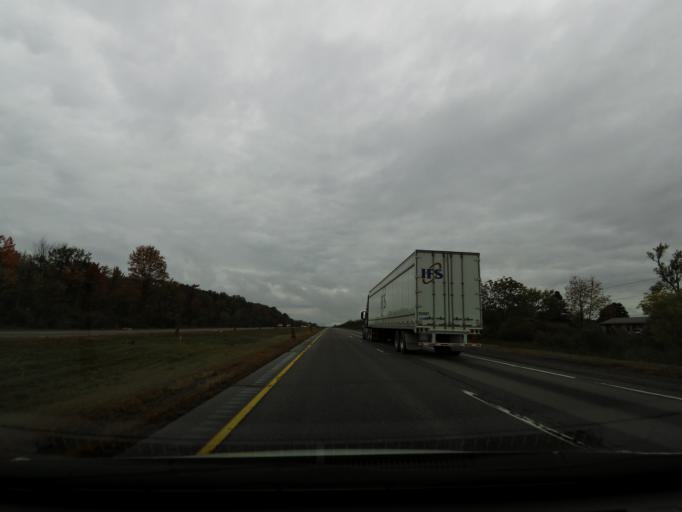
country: CA
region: Ontario
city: Prescott
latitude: 44.6849
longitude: -75.5877
